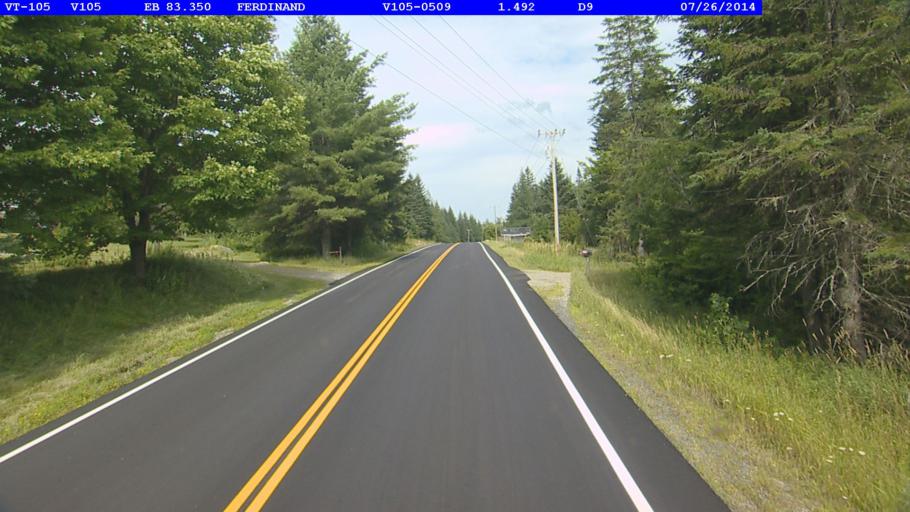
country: US
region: New Hampshire
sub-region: Coos County
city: Stratford
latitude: 44.7797
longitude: -71.7750
